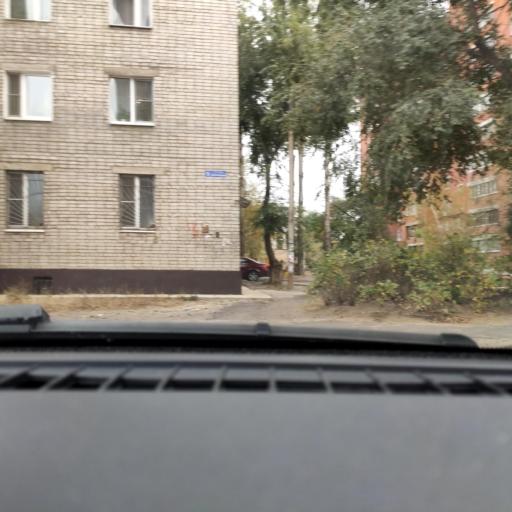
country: RU
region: Voronezj
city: Voronezh
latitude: 51.6448
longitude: 39.2703
